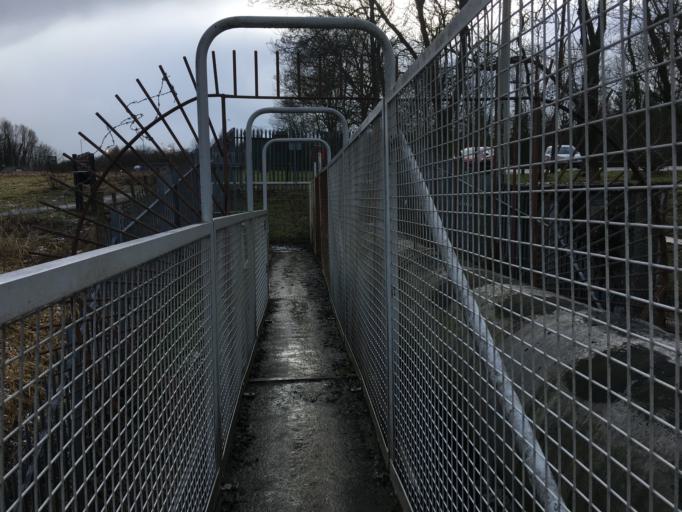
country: GB
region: Scotland
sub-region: Stirling
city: Bridge of Allan
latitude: 56.1359
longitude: -3.9700
